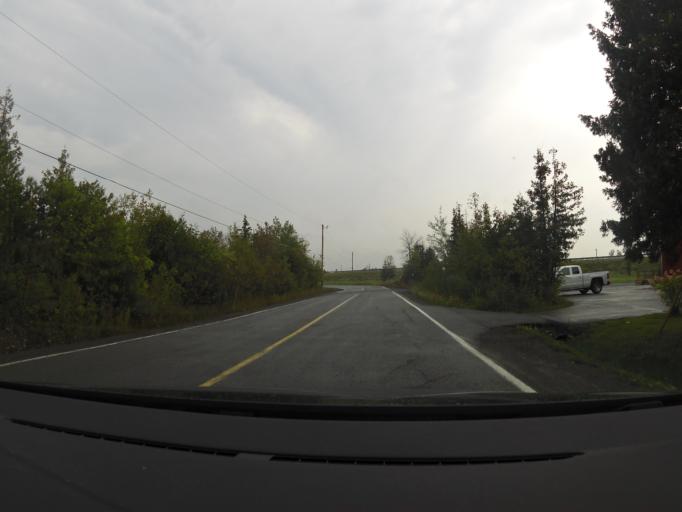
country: CA
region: Ontario
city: Carleton Place
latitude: 45.1783
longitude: -76.0488
